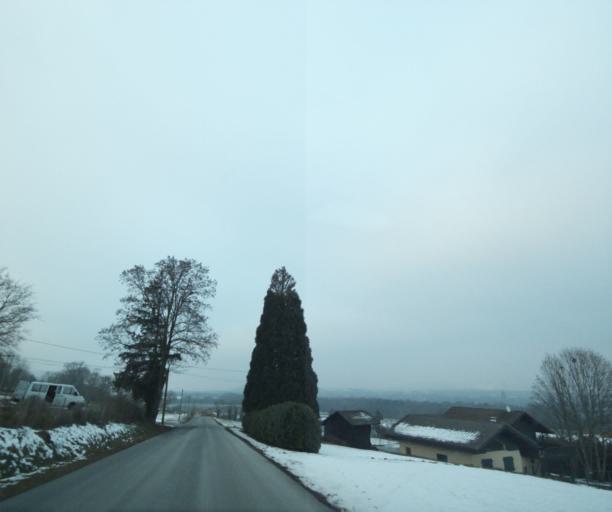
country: FR
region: Rhone-Alpes
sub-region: Departement de la Haute-Savoie
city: Reignier-Esery
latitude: 46.1335
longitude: 6.2567
